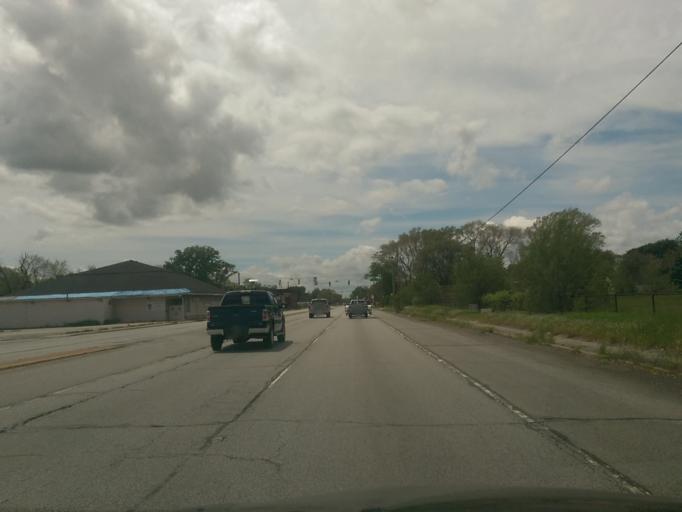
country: US
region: Indiana
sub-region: Lake County
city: Gary
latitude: 41.6020
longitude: -87.4042
